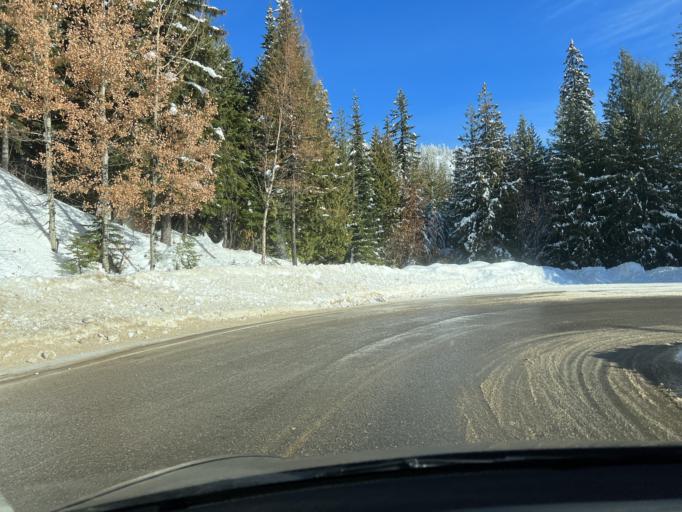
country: US
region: Idaho
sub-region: Bonner County
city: Ponderay
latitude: 48.3460
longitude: -116.5967
